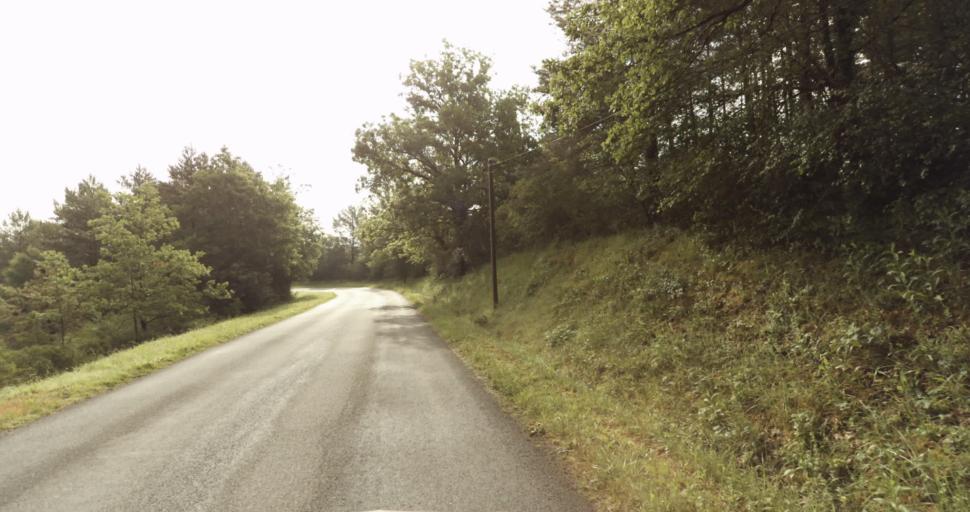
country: FR
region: Aquitaine
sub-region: Departement de la Dordogne
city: Lalinde
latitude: 44.9142
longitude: 0.7948
